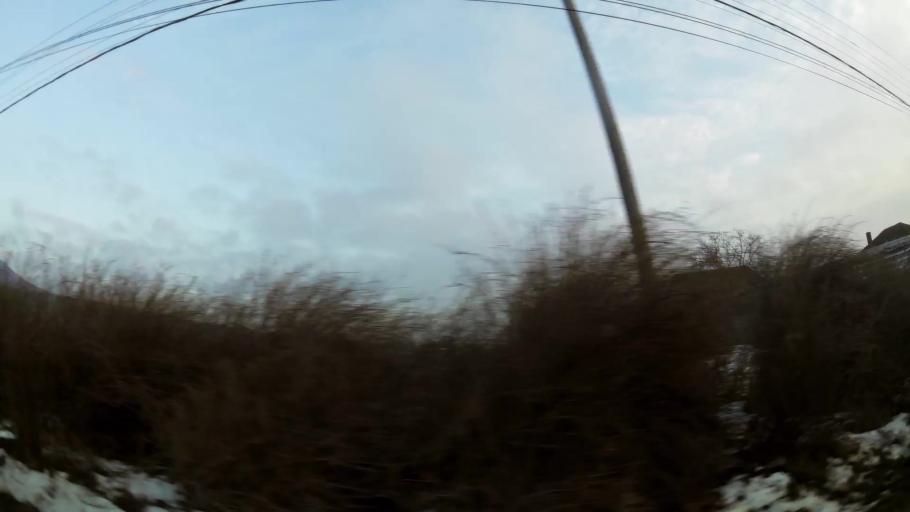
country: MK
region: Aracinovo
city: Arachinovo
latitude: 42.0311
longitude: 21.5479
